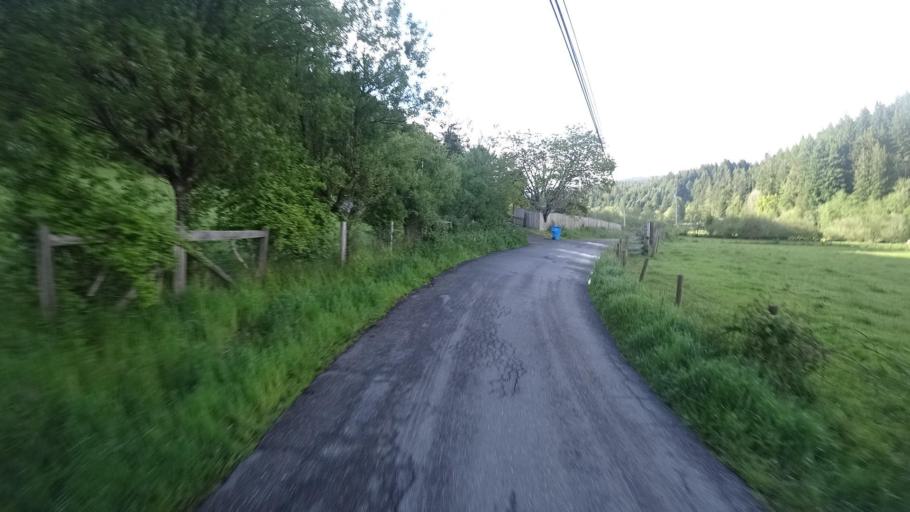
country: US
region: California
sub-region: Humboldt County
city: Arcata
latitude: 40.8925
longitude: -124.0411
